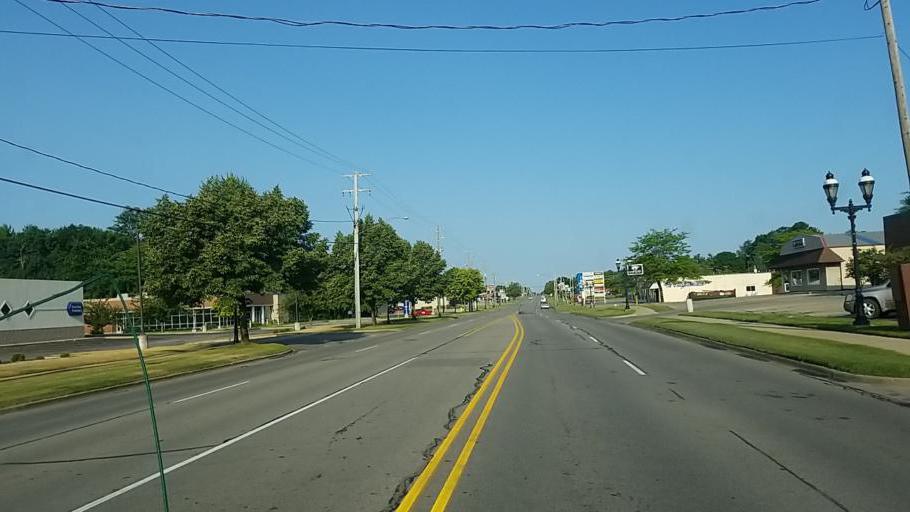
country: US
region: Michigan
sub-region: Newaygo County
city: Fremont
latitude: 43.4672
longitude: -85.9605
